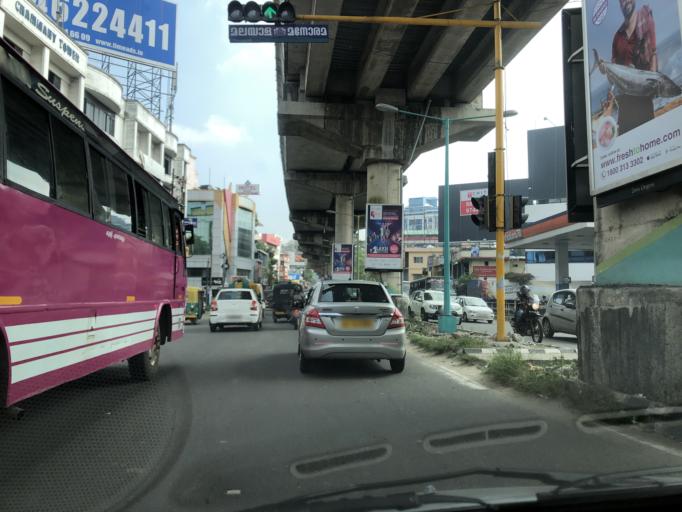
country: IN
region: Kerala
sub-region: Ernakulam
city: Cochin
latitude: 9.9951
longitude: 76.2922
